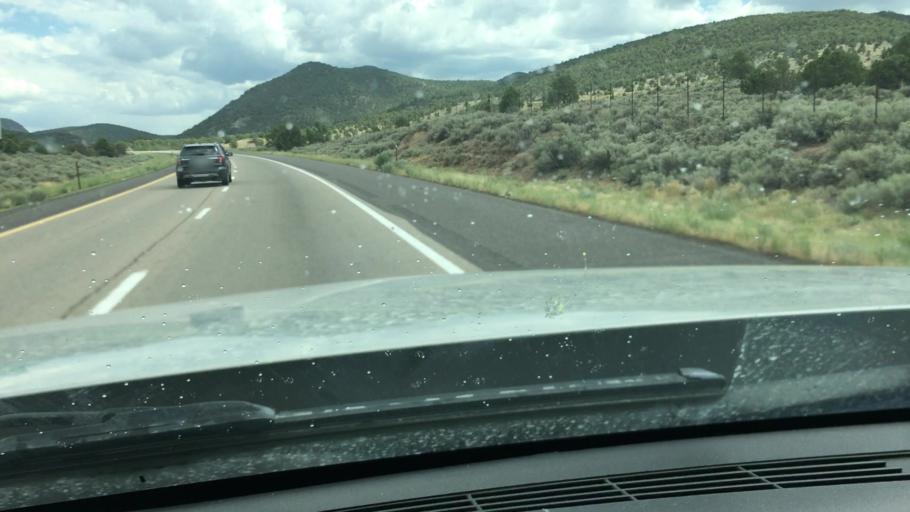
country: US
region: Utah
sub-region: Beaver County
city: Beaver
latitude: 38.1925
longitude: -112.6443
